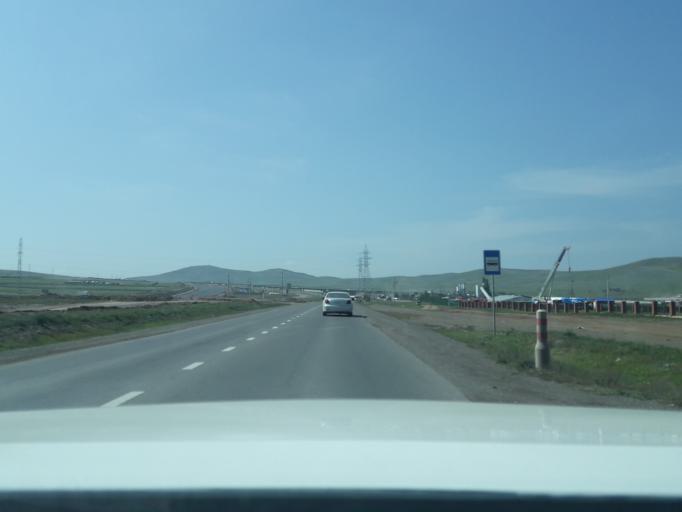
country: MN
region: Ulaanbaatar
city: Ulaanbaatar
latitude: 47.8221
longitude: 106.7628
